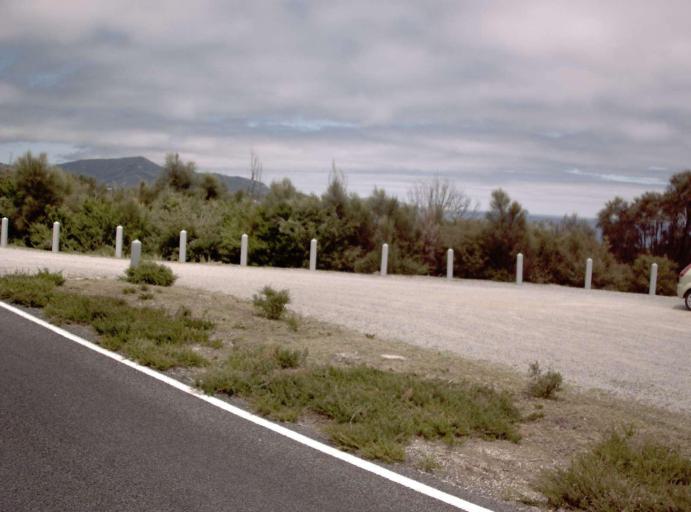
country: AU
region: Victoria
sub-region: Latrobe
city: Morwell
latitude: -39.0152
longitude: 146.2991
